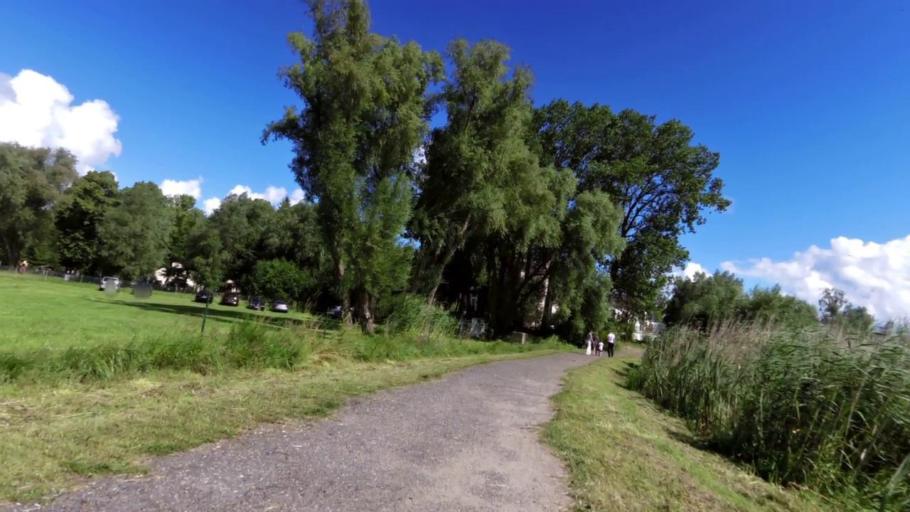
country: PL
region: West Pomeranian Voivodeship
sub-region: Powiat koszalinski
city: Mielno
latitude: 54.2638
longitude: 16.0792
